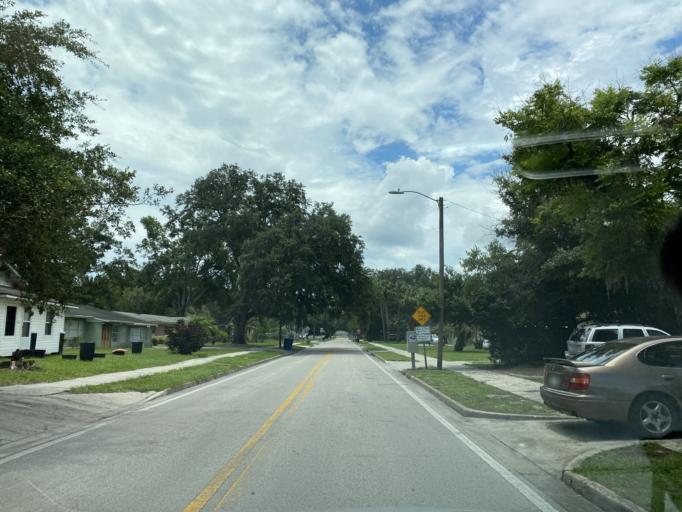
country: US
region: Florida
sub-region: Seminole County
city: Sanford
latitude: 28.7980
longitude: -81.2524
